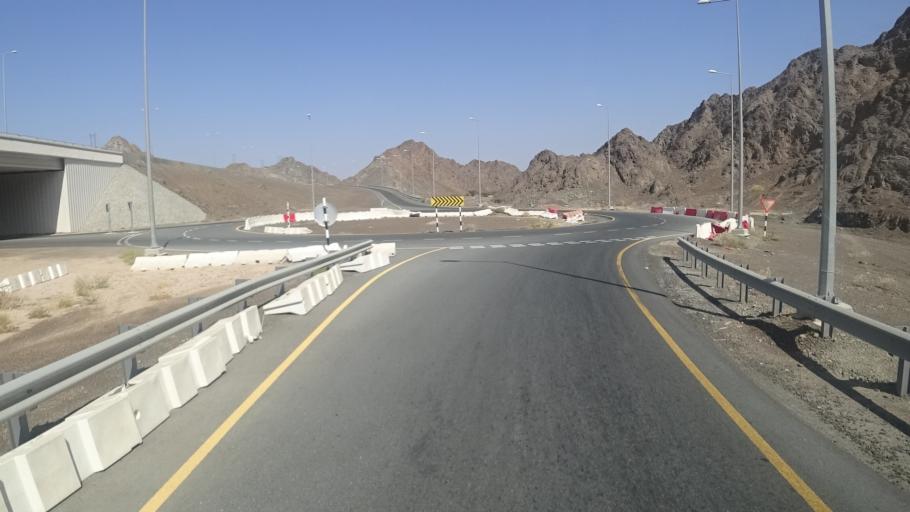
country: OM
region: Ash Sharqiyah
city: Ibra'
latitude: 22.6858
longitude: 58.5821
